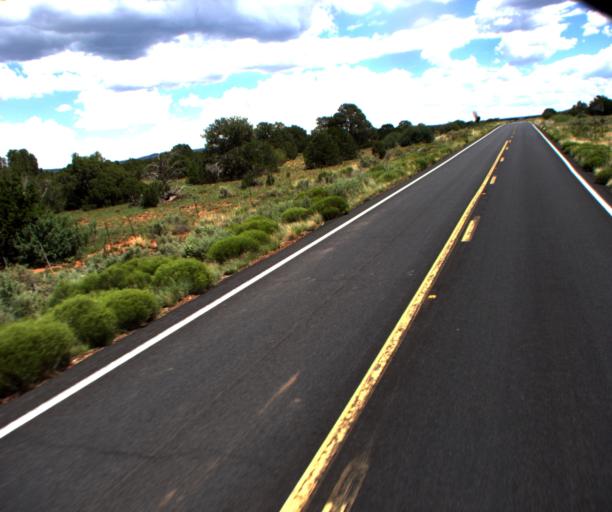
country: US
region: Arizona
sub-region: Coconino County
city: Parks
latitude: 35.6085
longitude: -112.0558
